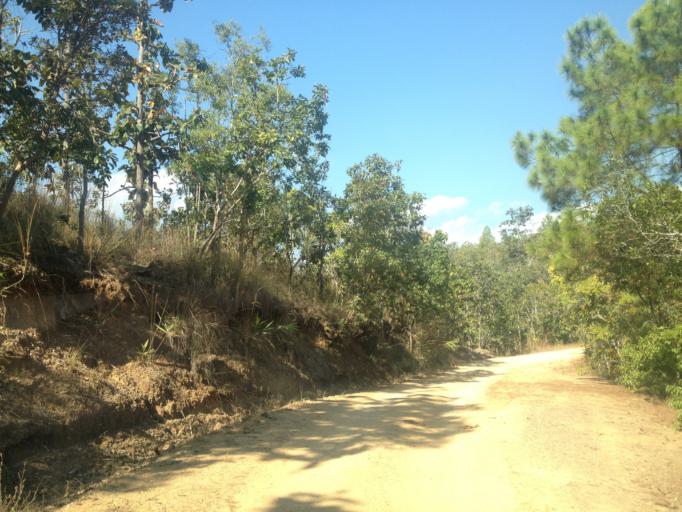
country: TH
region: Mae Hong Son
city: Ban Huai I Huak
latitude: 18.1204
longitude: 98.2052
